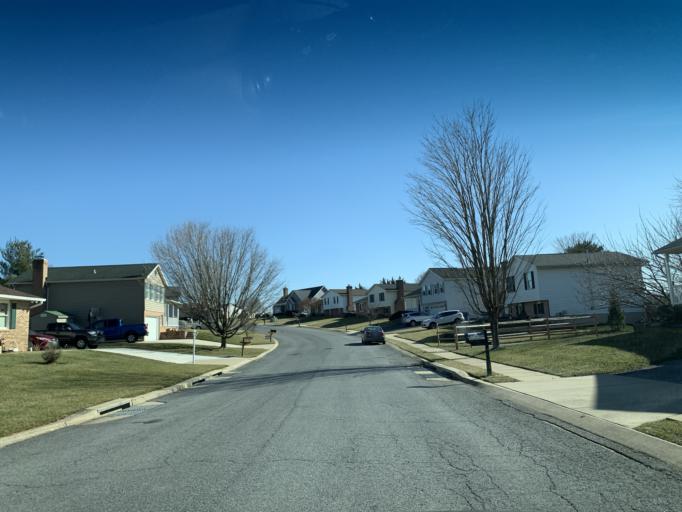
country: US
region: Maryland
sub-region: Carroll County
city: Westminster
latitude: 39.5960
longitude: -76.9947
